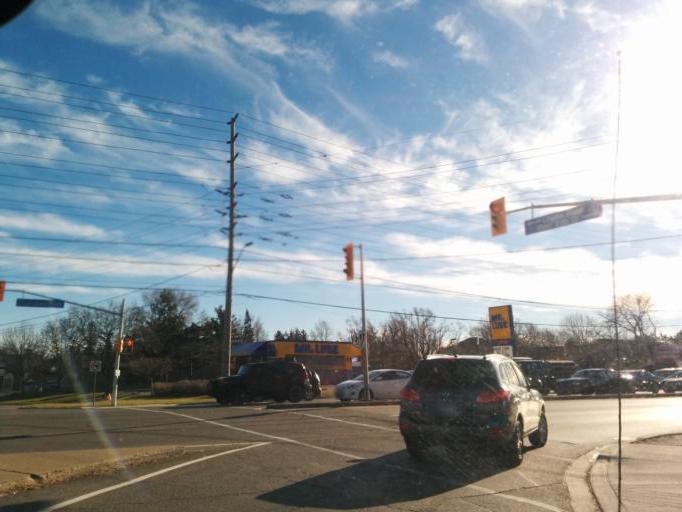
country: CA
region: Ontario
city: Mississauga
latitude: 43.5309
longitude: -79.6732
